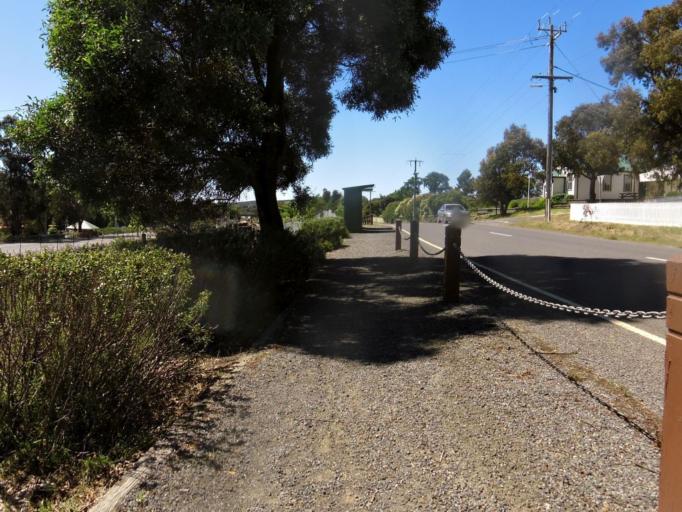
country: AU
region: Victoria
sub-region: Whittlesea
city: Whittlesea
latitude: -37.3571
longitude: 145.0273
